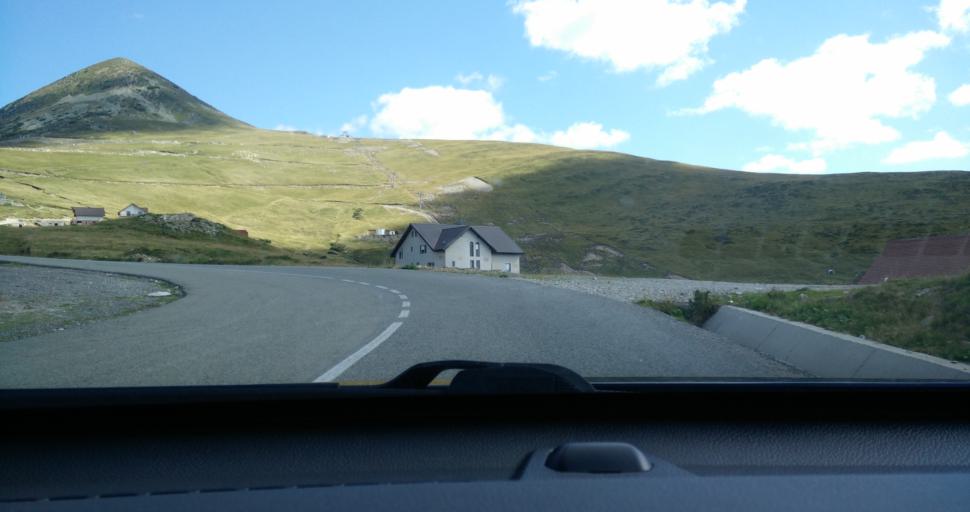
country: RO
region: Gorj
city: Novaci-Straini
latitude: 45.3115
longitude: 23.6827
